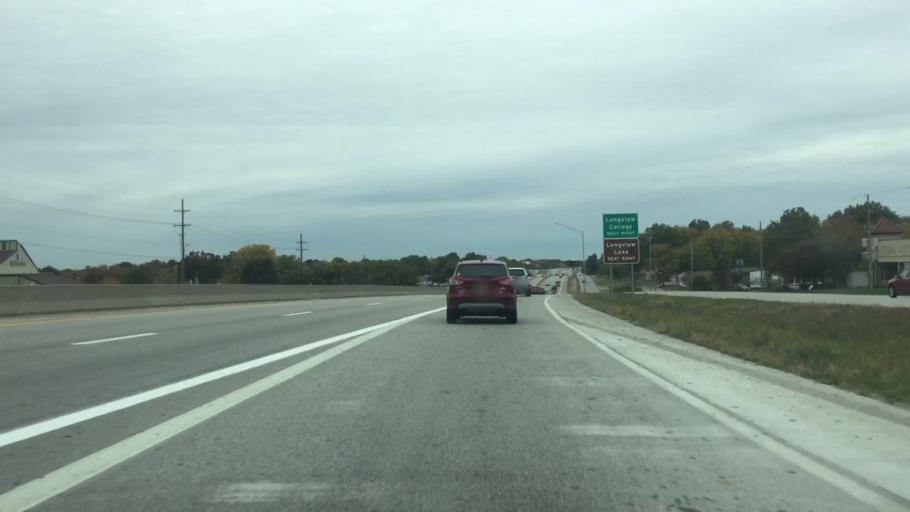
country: US
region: Missouri
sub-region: Jackson County
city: Lees Summit
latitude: 38.9043
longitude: -94.3805
